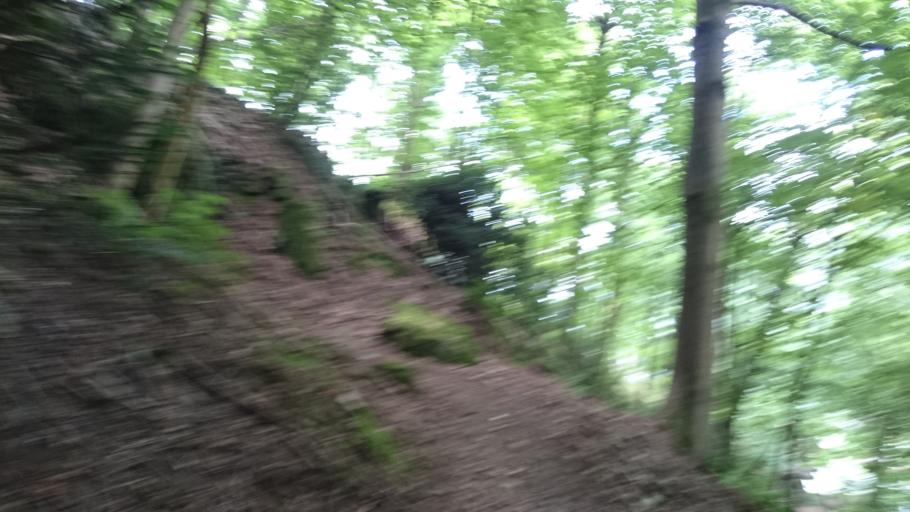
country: DE
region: Baden-Wuerttemberg
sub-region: Karlsruhe Region
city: Heidelberg
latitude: 49.4155
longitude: 8.7240
